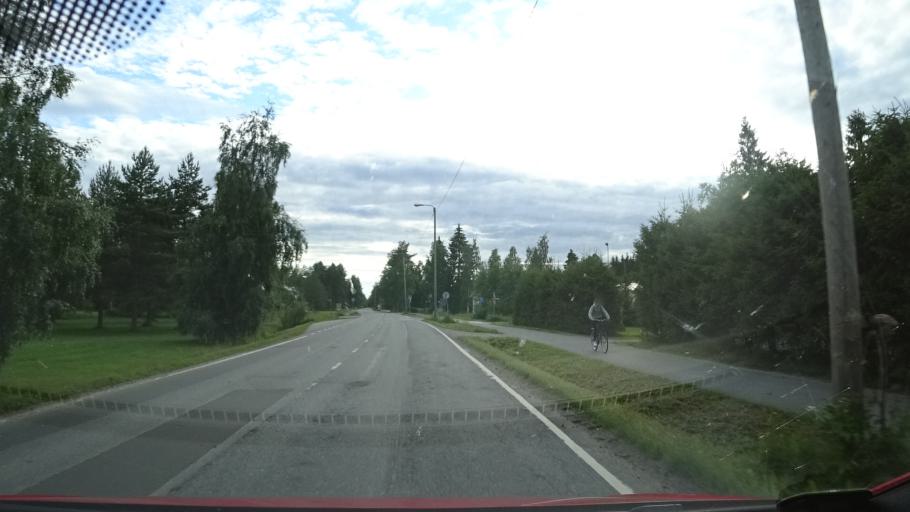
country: FI
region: Northern Ostrobothnia
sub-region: Oulu
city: Liminka
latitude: 64.8082
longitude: 25.4414
